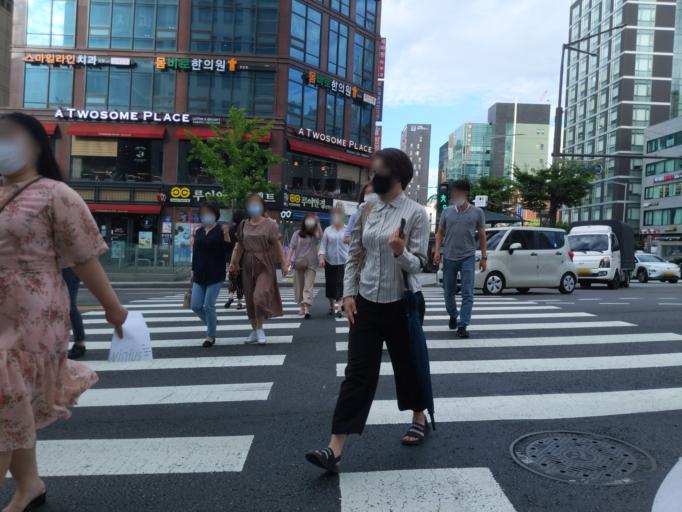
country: KR
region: Seoul
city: Seoul
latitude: 37.5075
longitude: 127.0336
